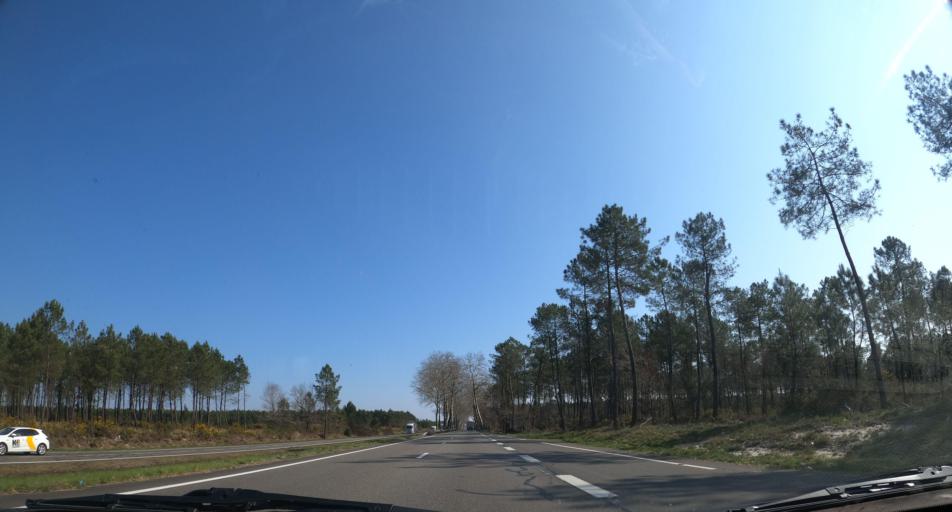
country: FR
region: Aquitaine
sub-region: Departement des Landes
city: Riviere-Saas-et-Gourby
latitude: 43.7053
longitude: -1.1720
